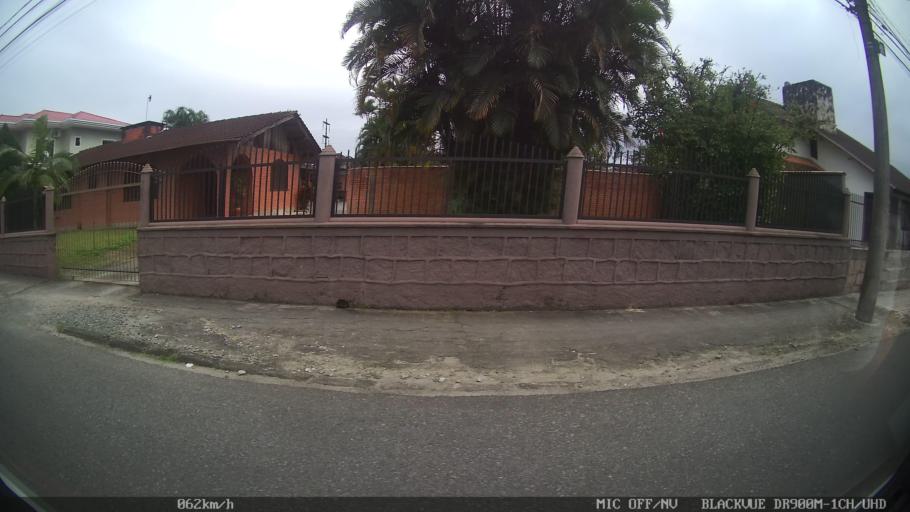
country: BR
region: Santa Catarina
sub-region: Joinville
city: Joinville
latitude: -26.2810
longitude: -48.8747
